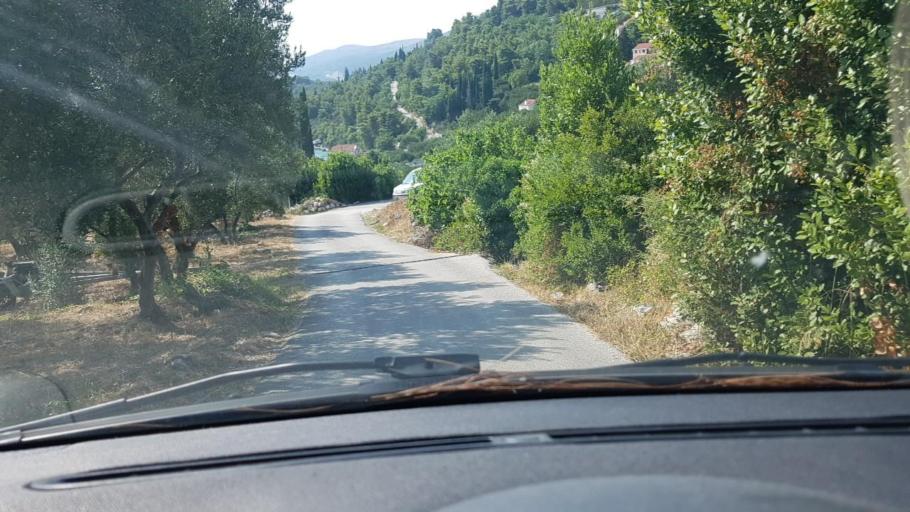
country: HR
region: Dubrovacko-Neretvanska
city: Podgora
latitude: 42.7829
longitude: 17.8623
